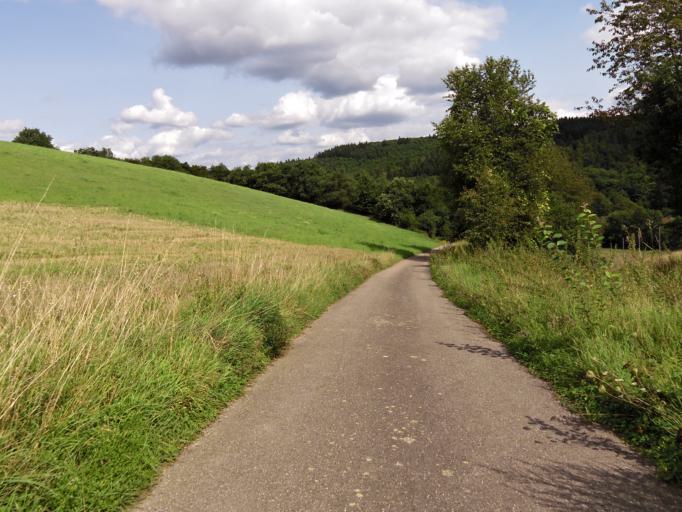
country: DE
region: Rheinland-Pfalz
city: Niederhausen an der Appel
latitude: 49.7621
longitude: 7.9037
